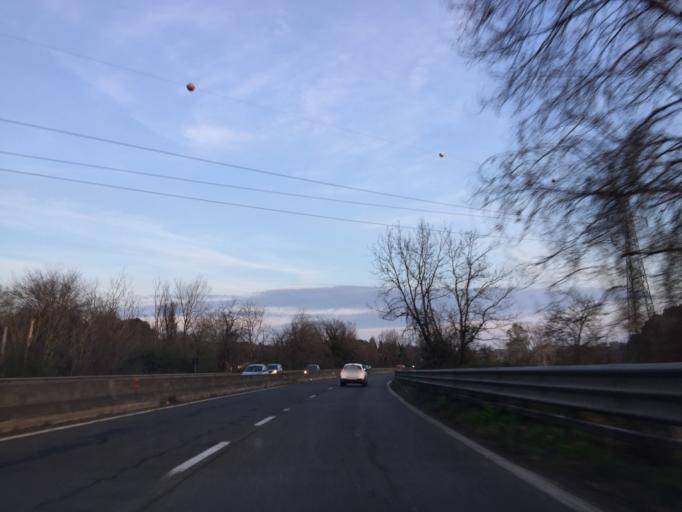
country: IT
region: Latium
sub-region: Citta metropolitana di Roma Capitale
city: Monte Caminetto
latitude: 41.9954
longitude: 12.4641
